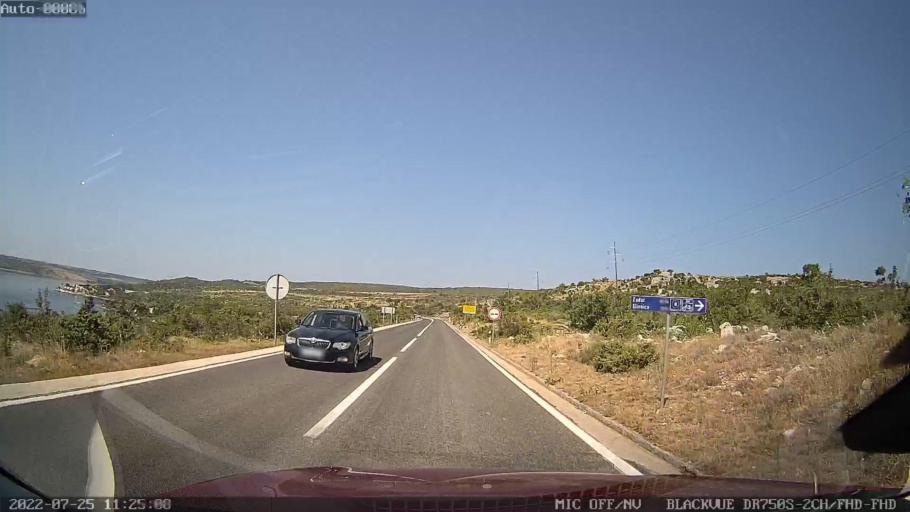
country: HR
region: Zadarska
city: Posedarje
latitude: 44.2224
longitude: 15.5254
